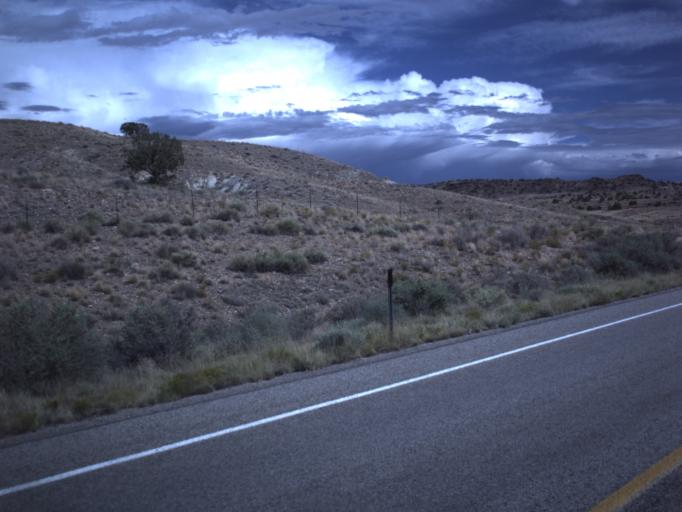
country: US
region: Colorado
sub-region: Montezuma County
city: Towaoc
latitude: 37.1964
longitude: -109.1482
